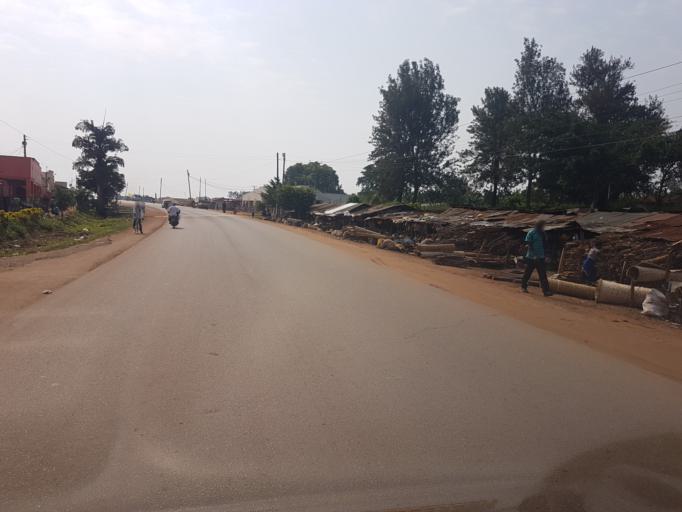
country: UG
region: Western Region
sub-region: Mbarara District
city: Mbarara
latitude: -0.6348
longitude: 30.6180
